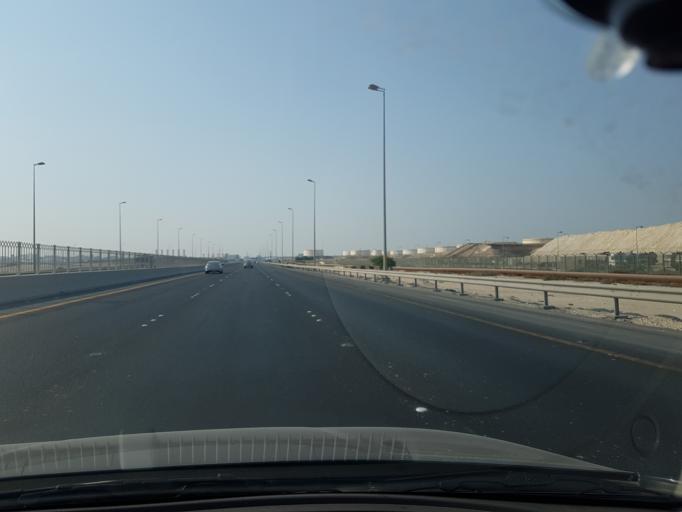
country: BH
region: Northern
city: Ar Rifa'
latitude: 26.1045
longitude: 50.6015
